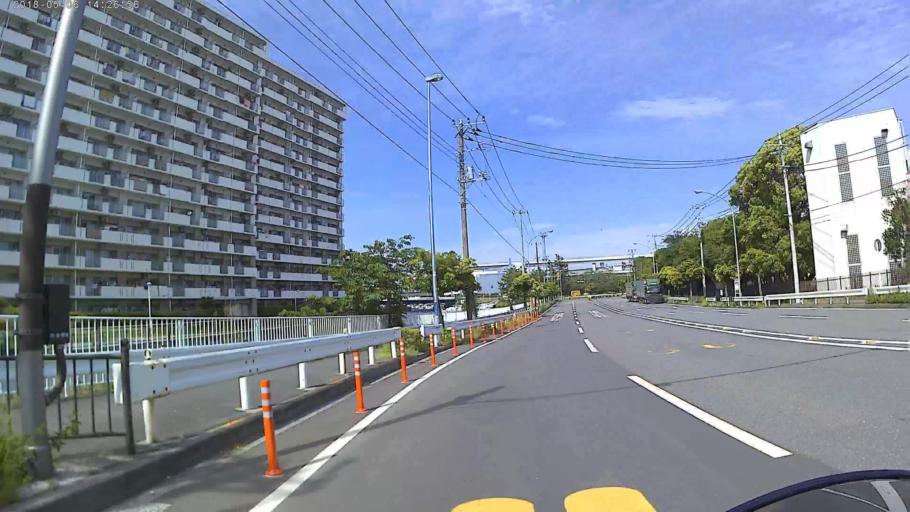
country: JP
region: Kanagawa
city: Yokohama
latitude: 35.4329
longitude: 139.6650
